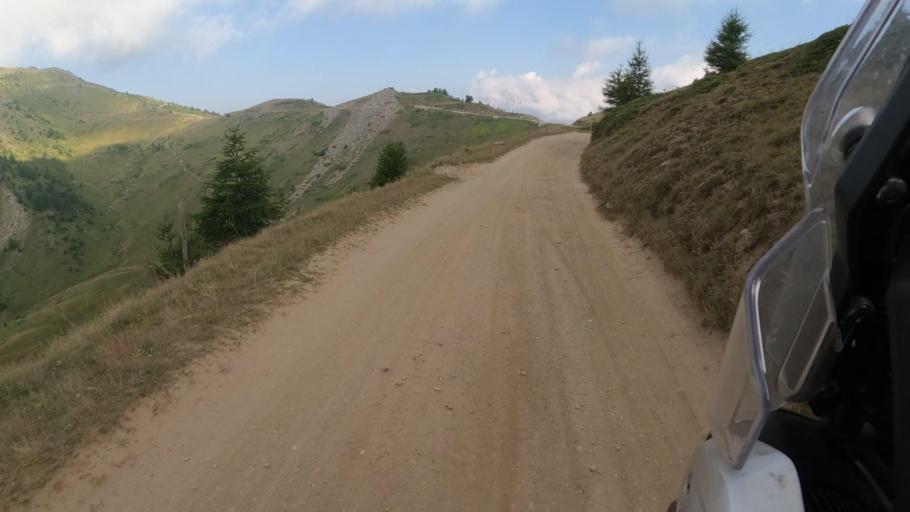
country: IT
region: Piedmont
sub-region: Provincia di Torino
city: Pragelato-Rua
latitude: 45.0355
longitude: 6.9187
